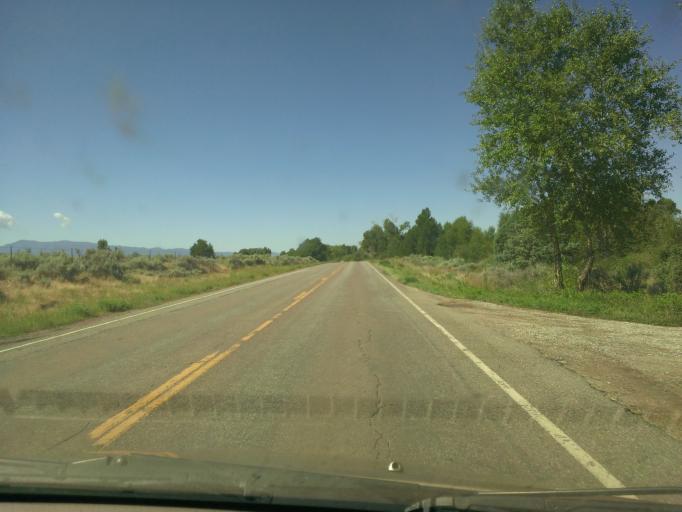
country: US
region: New Mexico
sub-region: Taos County
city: Arroyo Seco
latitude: 36.5072
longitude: -105.5857
